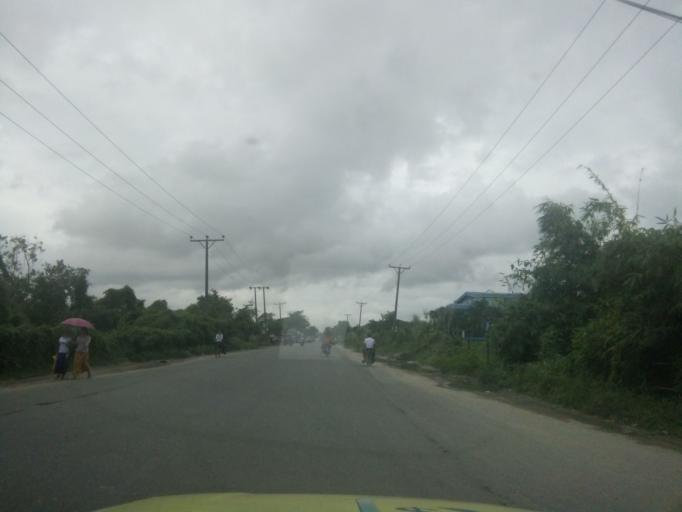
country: MM
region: Yangon
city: Yangon
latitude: 16.9132
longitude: 96.0515
